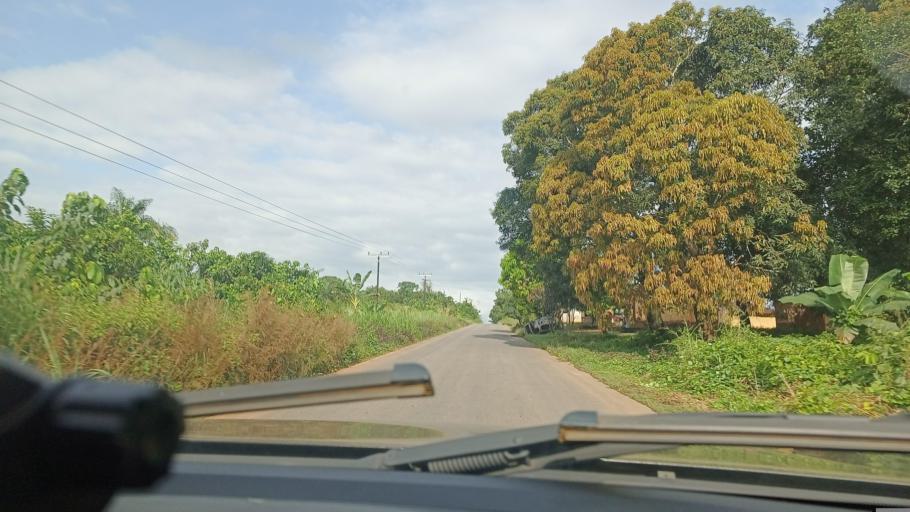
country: LR
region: Bomi
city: Tubmanburg
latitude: 6.7079
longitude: -10.9286
